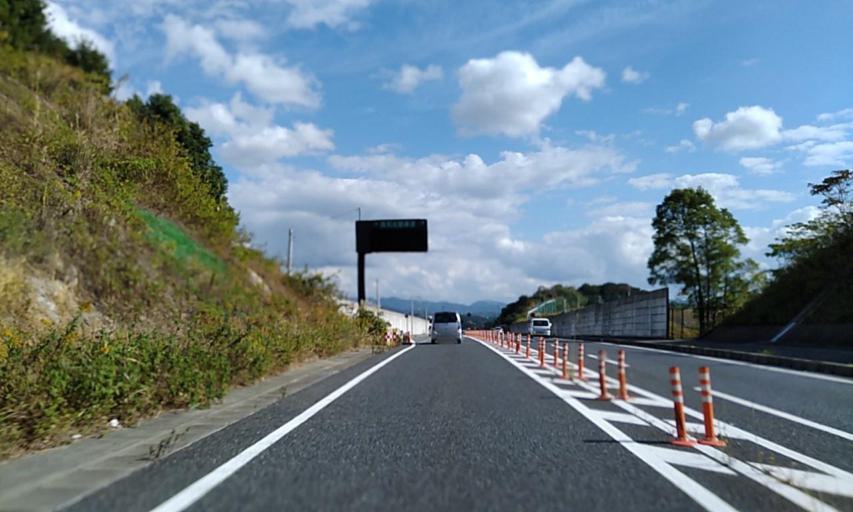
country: JP
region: Wakayama
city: Tanabe
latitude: 33.7481
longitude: 135.3635
